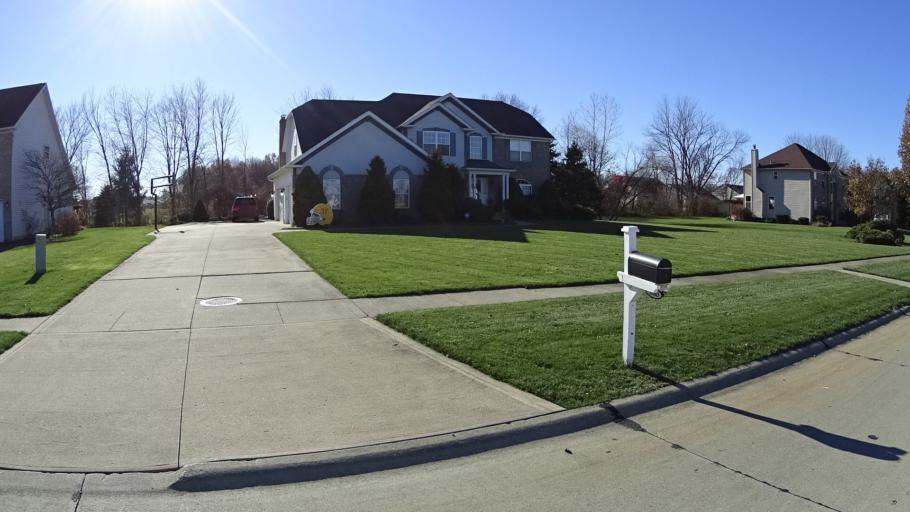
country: US
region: Ohio
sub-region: Lorain County
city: Sheffield
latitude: 41.4193
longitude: -82.0572
